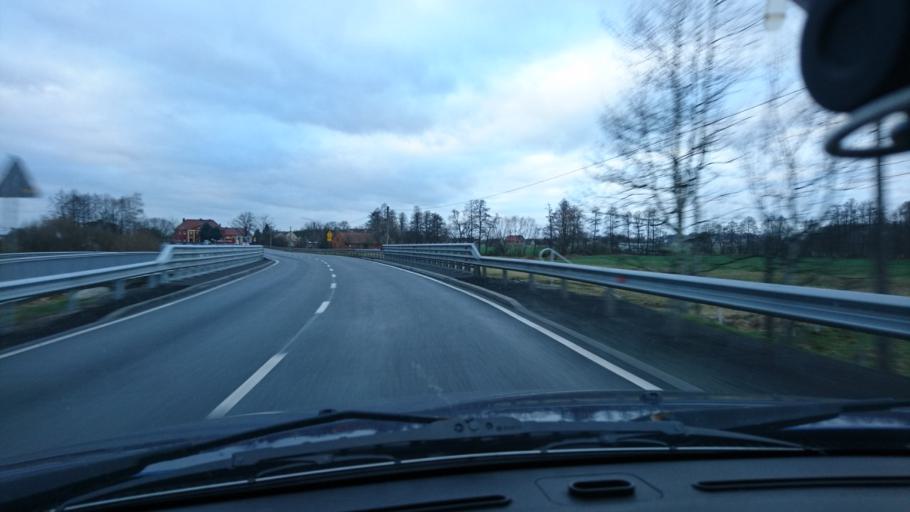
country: PL
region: Greater Poland Voivodeship
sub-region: Powiat kepinski
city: Opatow
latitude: 51.1643
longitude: 18.1519
